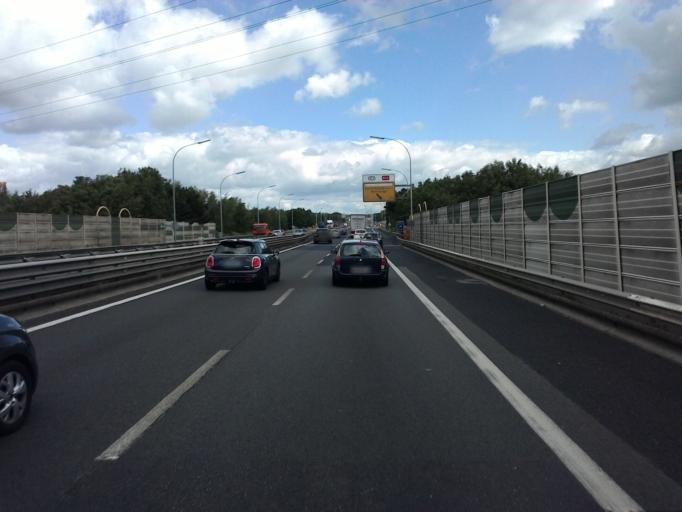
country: LU
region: Luxembourg
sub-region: Canton de Luxembourg
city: Strassen
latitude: 49.6042
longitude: 6.0807
